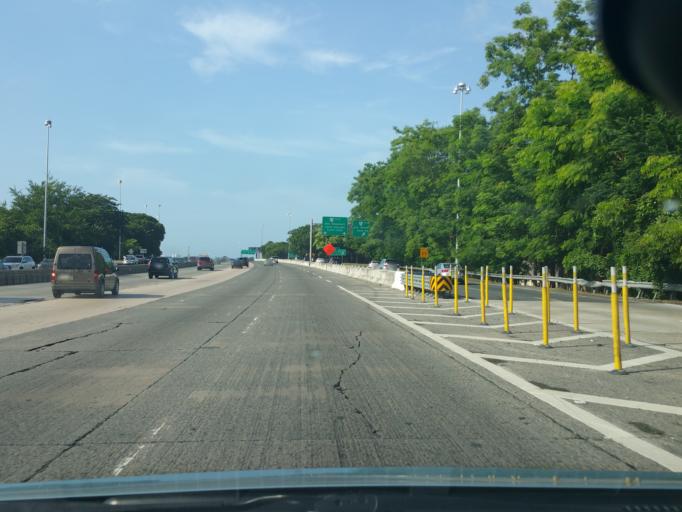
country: PR
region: Catano
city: Catano
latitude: 18.4146
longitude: -66.0700
